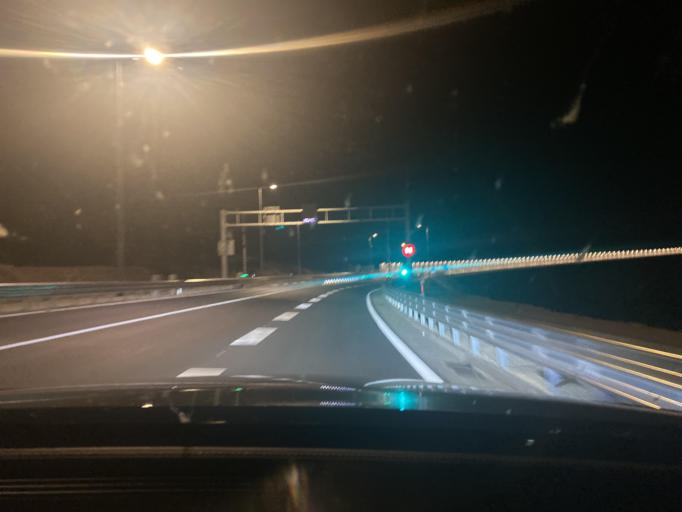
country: BA
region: Federation of Bosnia and Herzegovina
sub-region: Hercegovacko-Bosanski Kanton
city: Neum
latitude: 42.9425
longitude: 17.5428
